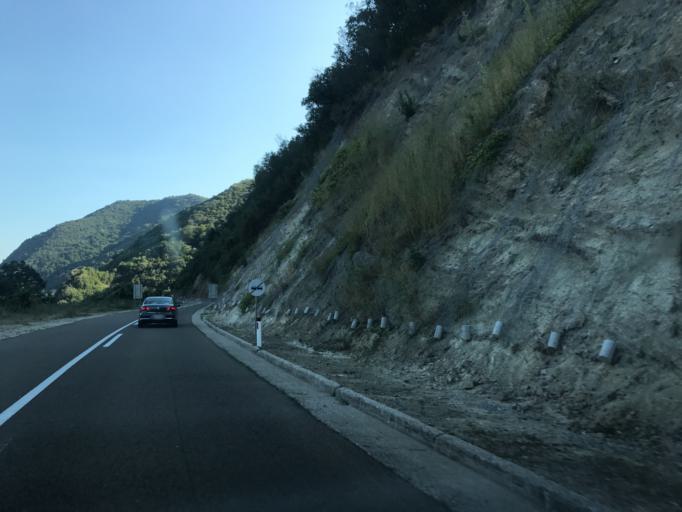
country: RO
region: Caras-Severin
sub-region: Comuna Berzasca
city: Berzasca
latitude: 44.5788
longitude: 22.0186
